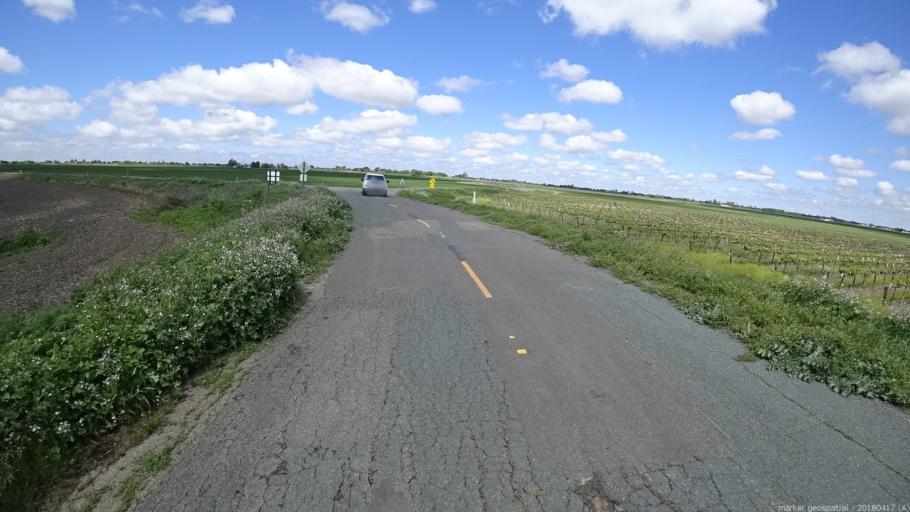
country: US
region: California
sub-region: Sacramento County
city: Walnut Grove
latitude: 38.2044
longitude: -121.5279
